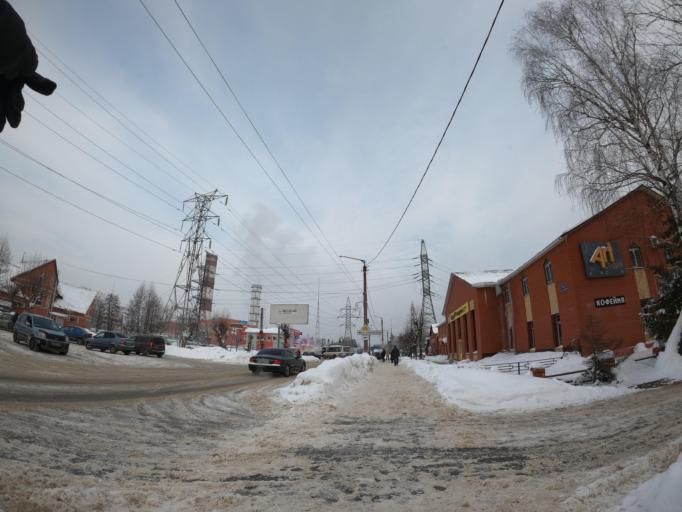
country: RU
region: Moskovskaya
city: Elektrogorsk
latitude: 55.8840
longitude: 38.7856
